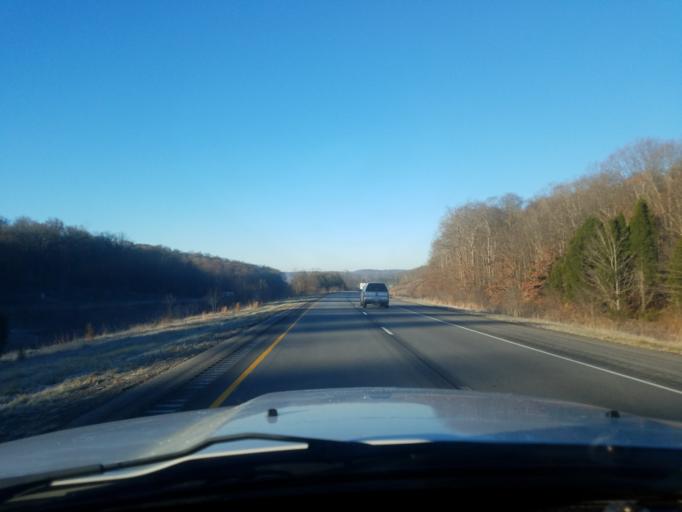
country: US
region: Indiana
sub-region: Dubois County
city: Ferdinand
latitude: 38.2315
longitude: -86.6811
